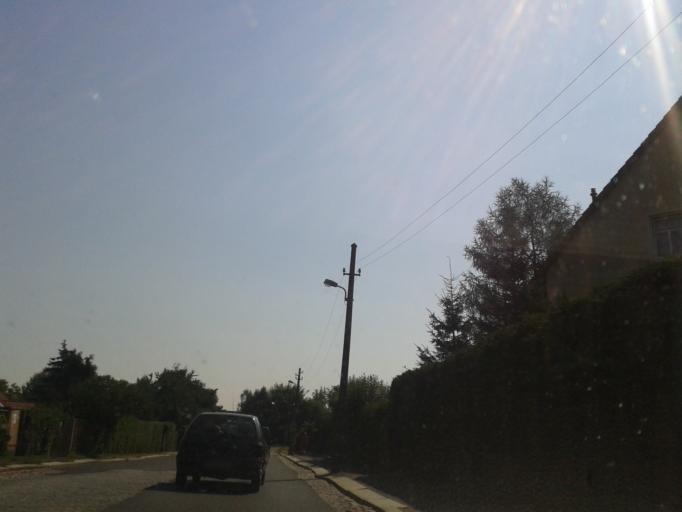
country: DE
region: Saxony
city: Freital
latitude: 51.0356
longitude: 13.6843
